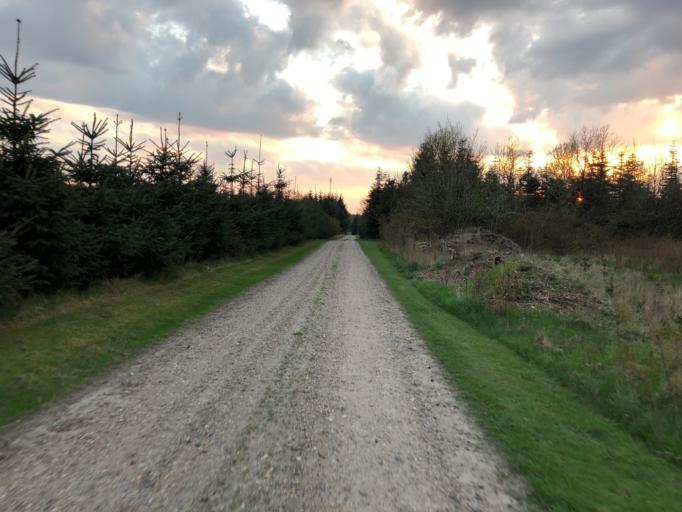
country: DK
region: Central Jutland
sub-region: Holstebro Kommune
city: Ulfborg
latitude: 56.2248
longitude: 8.4183
